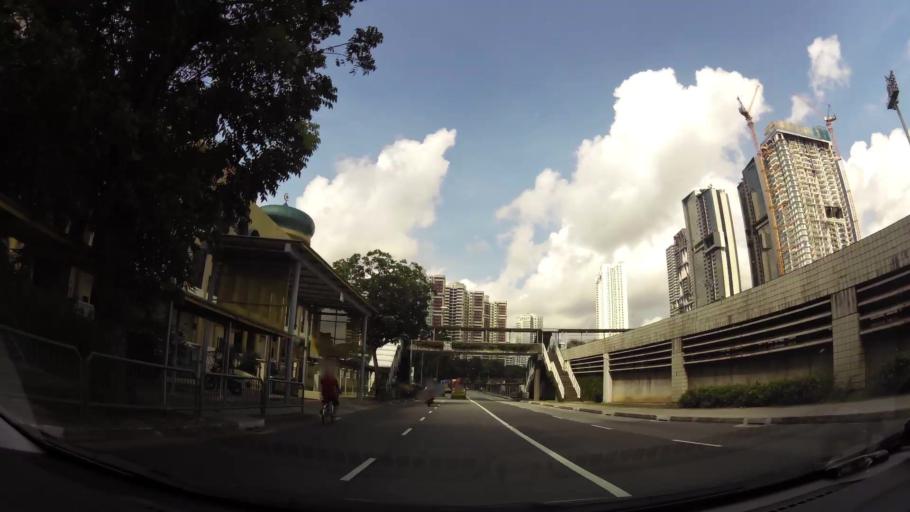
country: SG
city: Singapore
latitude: 1.2886
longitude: 103.8205
